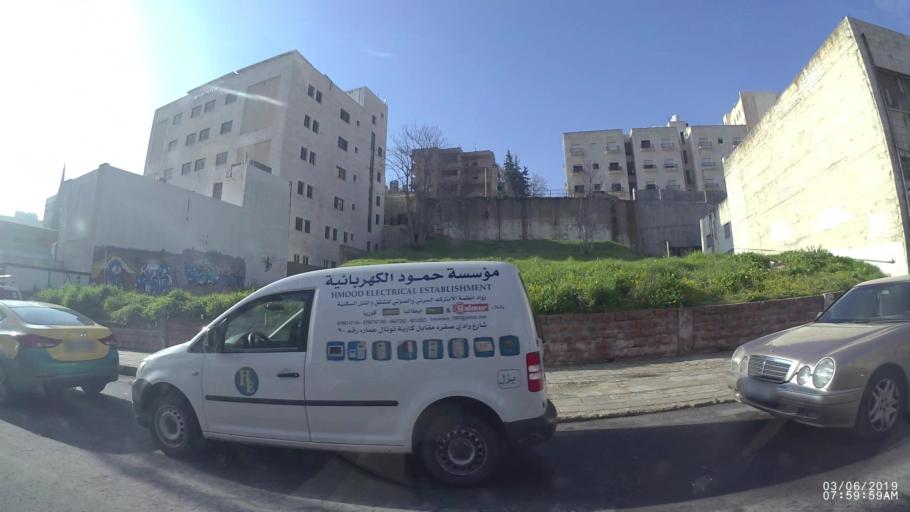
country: JO
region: Amman
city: Amman
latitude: 31.9566
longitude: 35.9130
